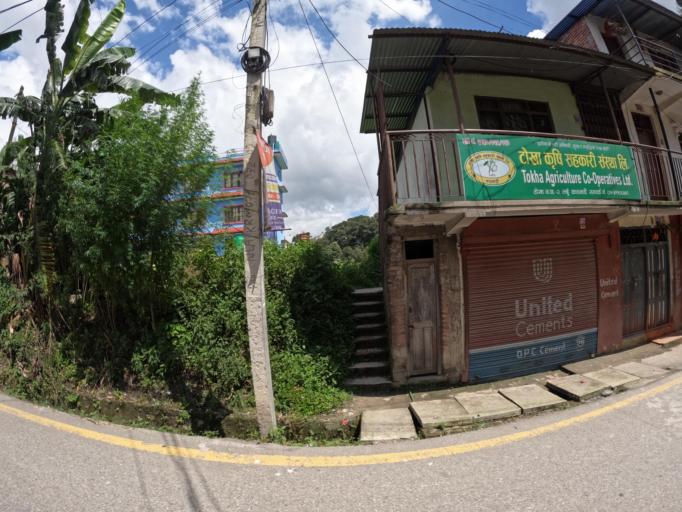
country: NP
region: Central Region
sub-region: Bagmati Zone
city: Kathmandu
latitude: 27.7722
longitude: 85.3302
